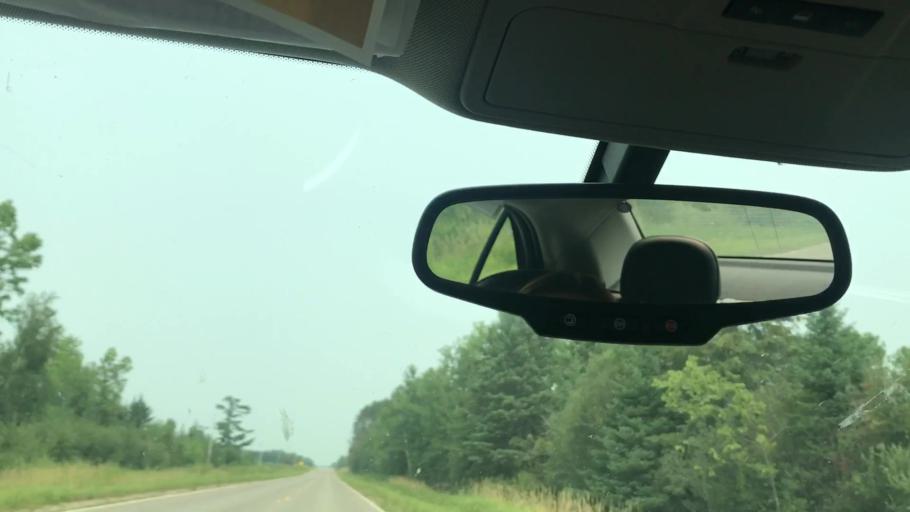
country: US
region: Minnesota
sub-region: Itasca County
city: Cohasset
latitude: 47.3721
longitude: -93.8803
